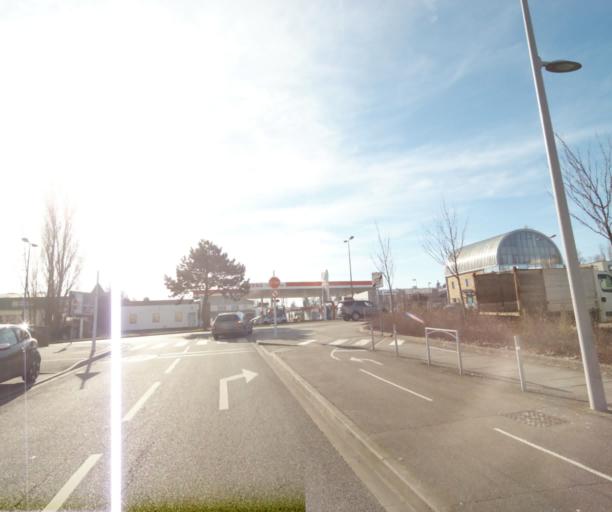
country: FR
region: Lorraine
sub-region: Departement de Meurthe-et-Moselle
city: Vandoeuvre-les-Nancy
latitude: 48.6601
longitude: 6.1829
